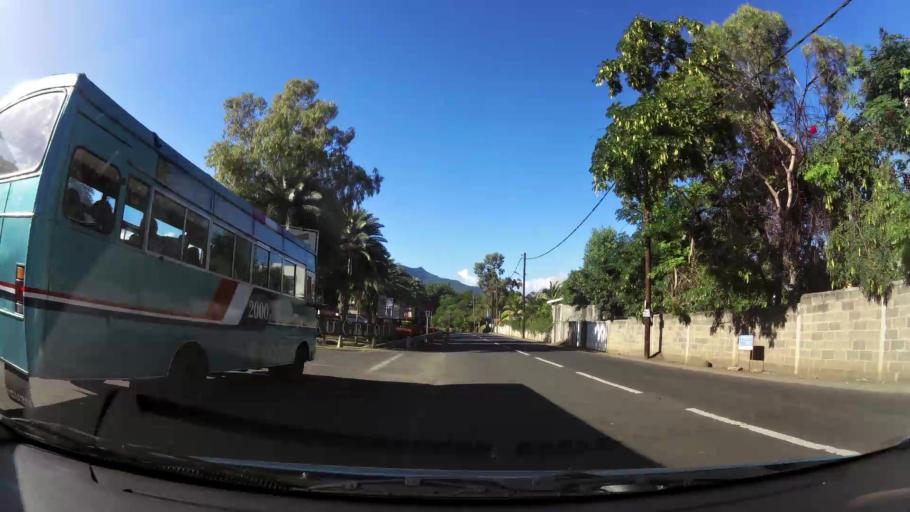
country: MU
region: Black River
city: Grande Riviere Noire
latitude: -20.3573
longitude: 57.3675
